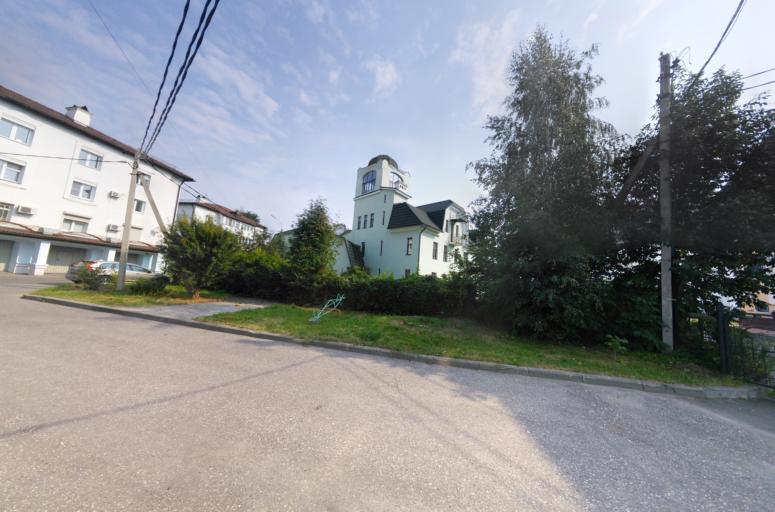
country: RU
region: Jaroslavl
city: Yaroslavl
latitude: 57.6344
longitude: 39.8866
